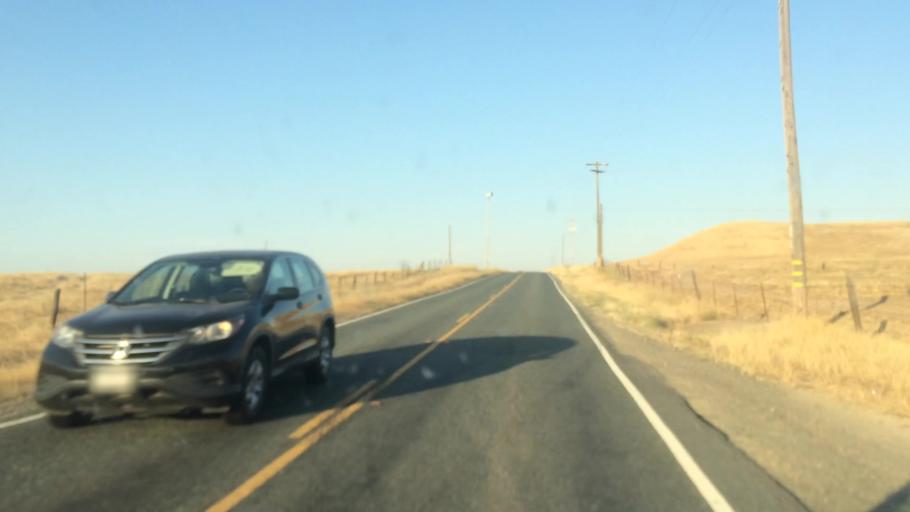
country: US
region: California
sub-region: Sacramento County
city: Clay
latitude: 38.3543
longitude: -121.0756
